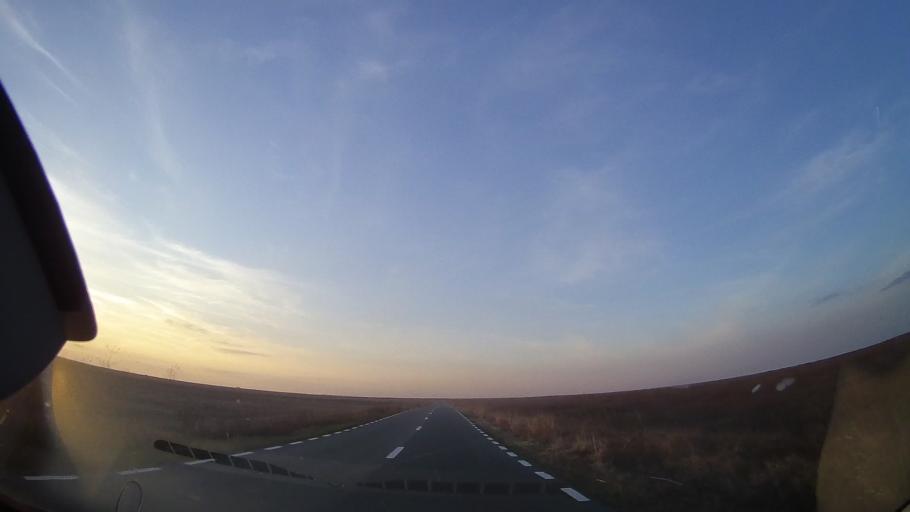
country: RO
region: Constanta
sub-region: Comuna Topraisar
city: Topraisar
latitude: 44.0145
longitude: 28.4348
